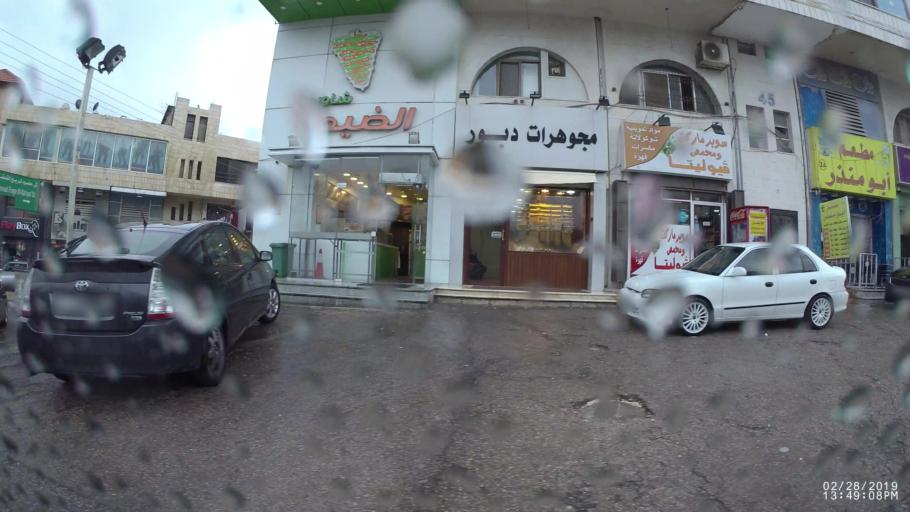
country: JO
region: Amman
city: Al Jubayhah
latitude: 32.0220
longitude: 35.8722
